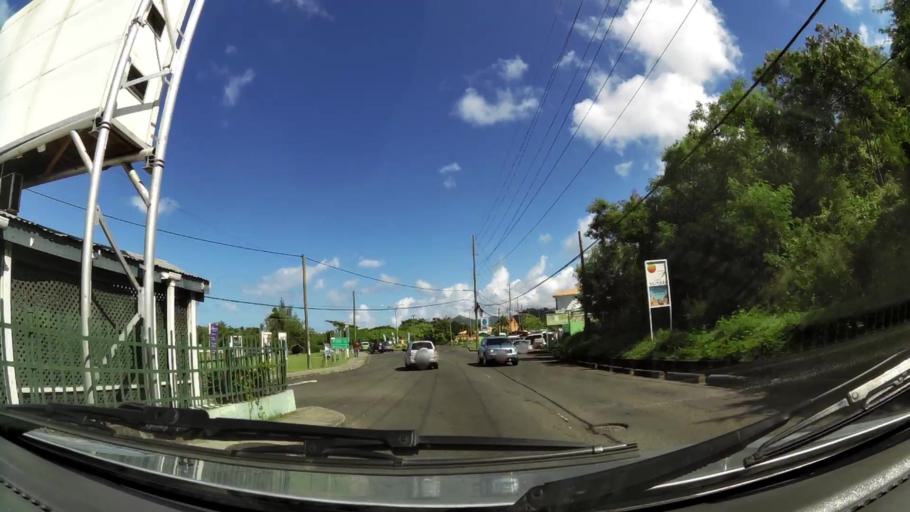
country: GD
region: Saint George
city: Saint George's
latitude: 12.0218
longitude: -61.7592
